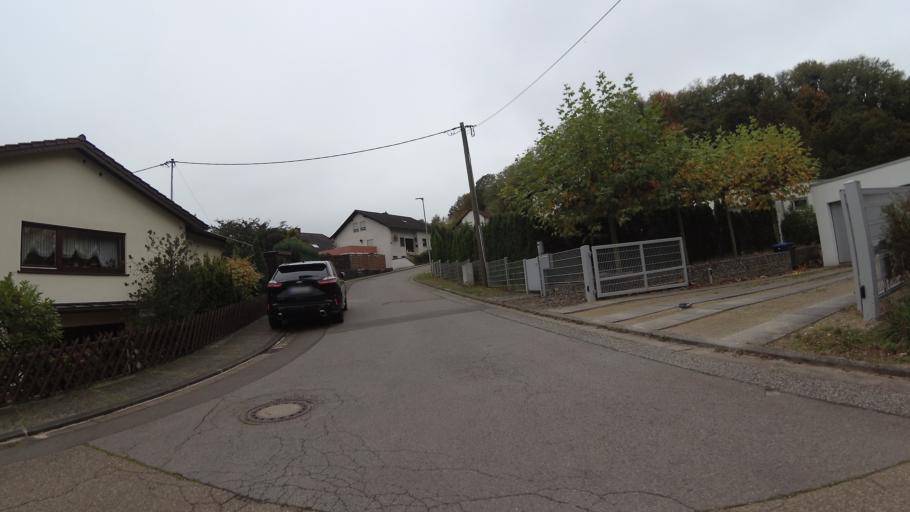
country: DE
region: Saarland
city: Blieskastel
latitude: 49.2658
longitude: 7.2761
